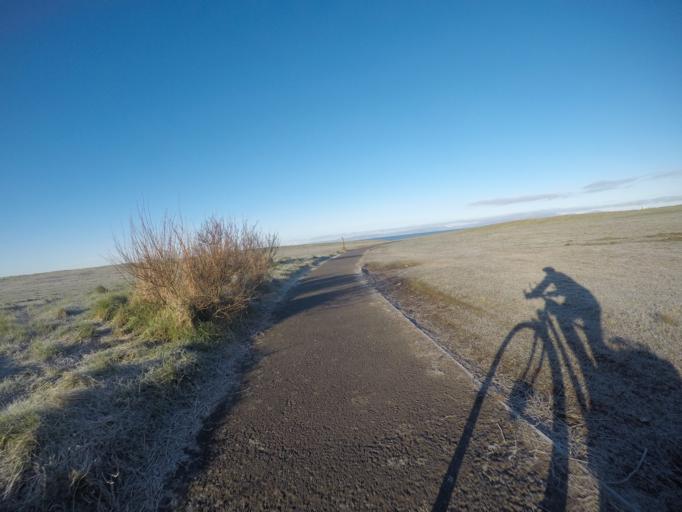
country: GB
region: Scotland
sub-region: North Ayrshire
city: Stevenston
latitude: 55.6260
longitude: -4.7460
